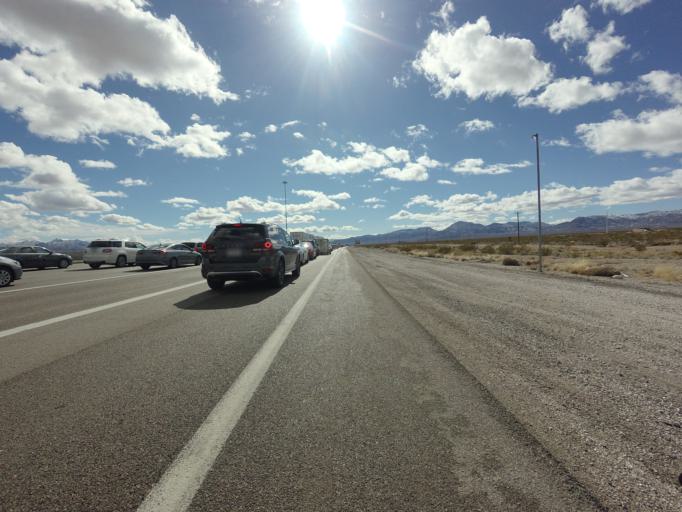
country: US
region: Nevada
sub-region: Clark County
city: Enterprise
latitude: 35.7781
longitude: -115.3307
